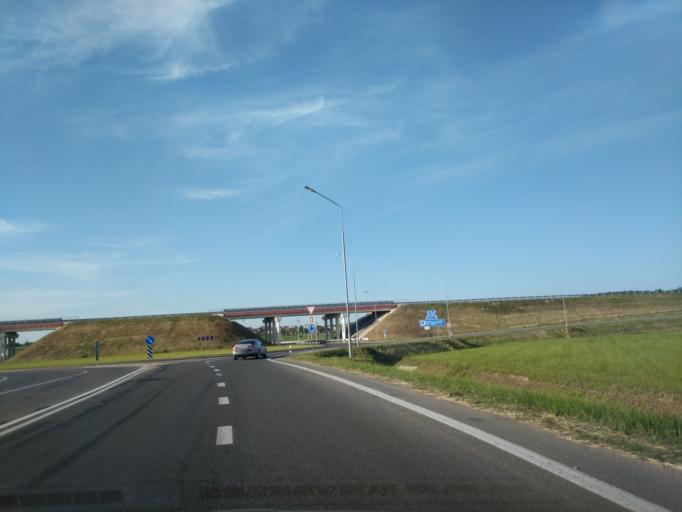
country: BY
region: Grodnenskaya
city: Ashmyany
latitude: 54.4346
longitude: 25.9658
